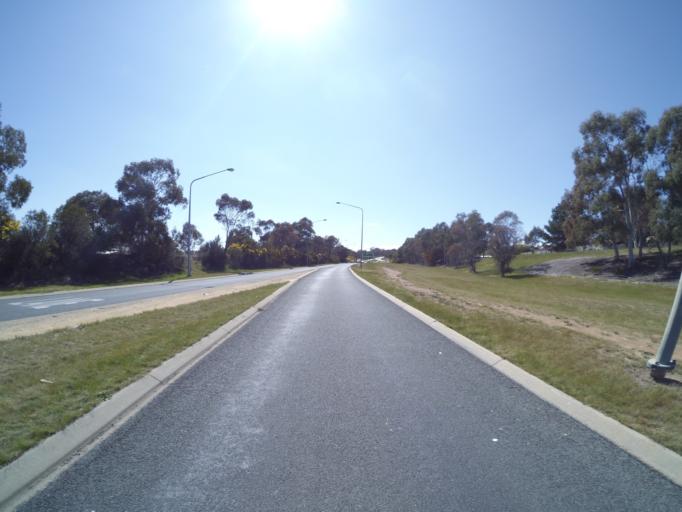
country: AU
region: Australian Capital Territory
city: Macarthur
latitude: -35.4368
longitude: 149.0926
